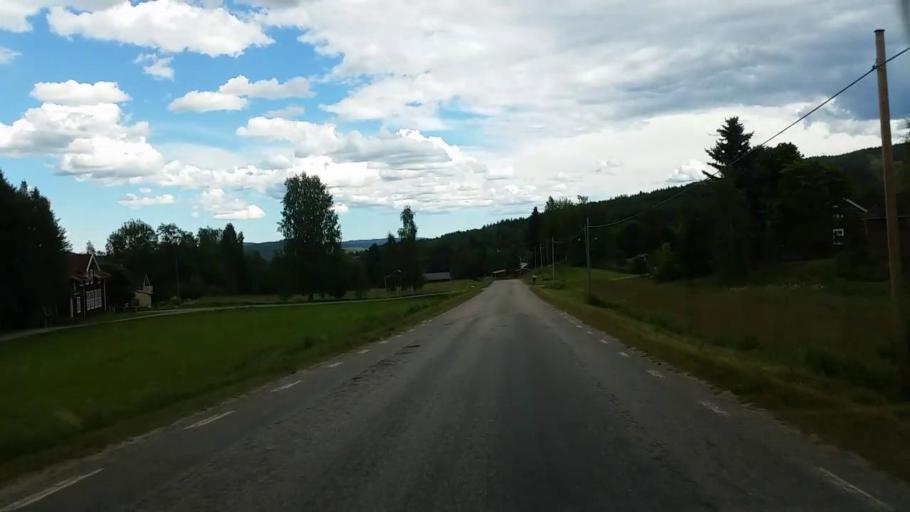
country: SE
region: Gaevleborg
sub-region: Ljusdals Kommun
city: Jaervsoe
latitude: 61.6678
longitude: 16.0791
